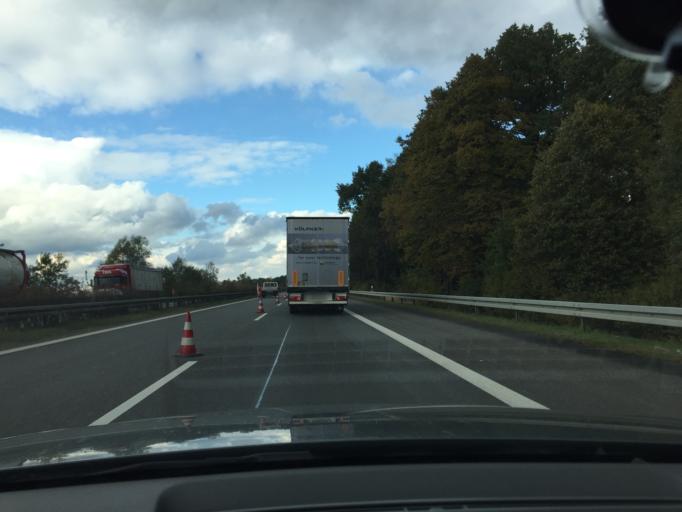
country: DE
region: Brandenburg
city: Bronkow
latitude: 51.6231
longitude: 13.9454
